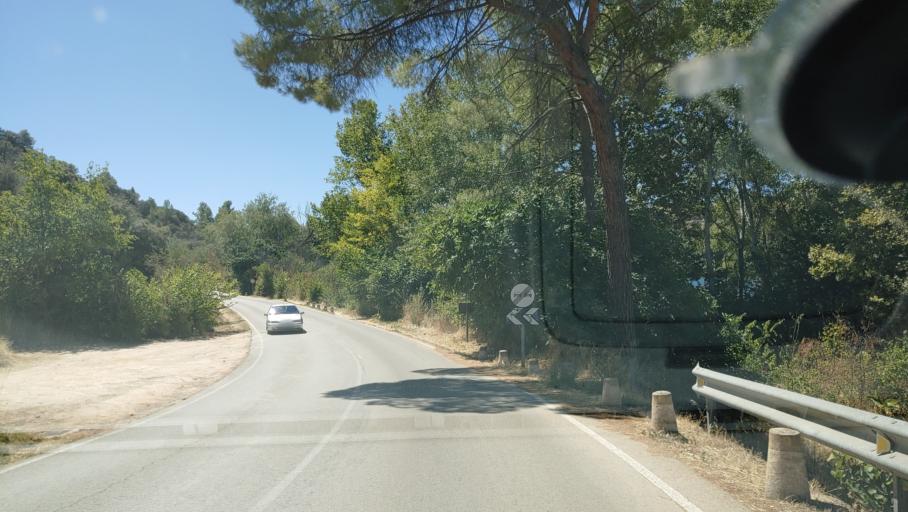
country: ES
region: Castille-La Mancha
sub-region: Provincia de Ciudad Real
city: Ruidera
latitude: 38.9554
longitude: -2.8608
